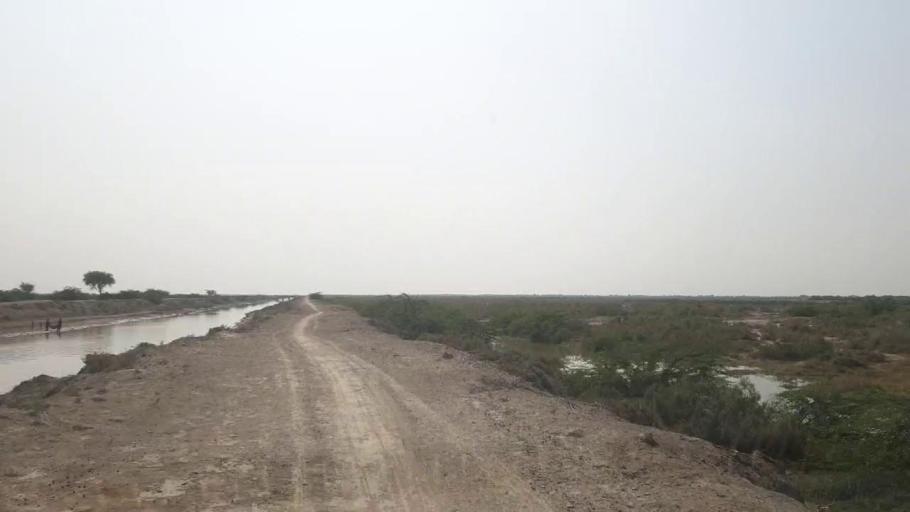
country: PK
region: Sindh
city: Kadhan
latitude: 24.3858
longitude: 68.9000
